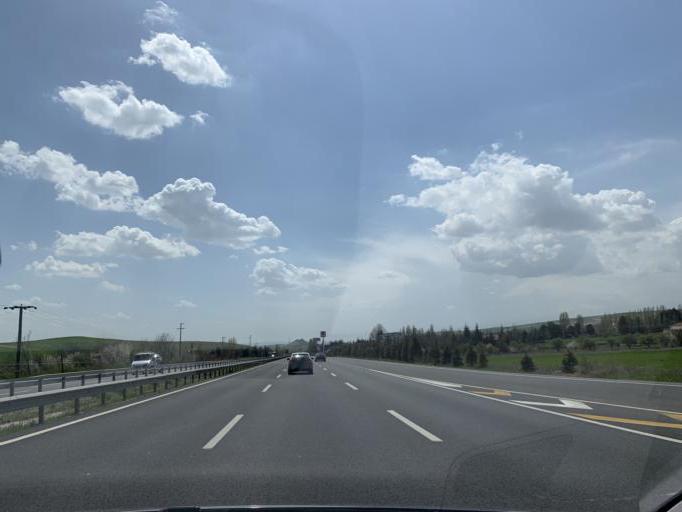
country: TR
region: Ankara
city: Etimesgut
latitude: 39.7992
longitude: 32.5379
